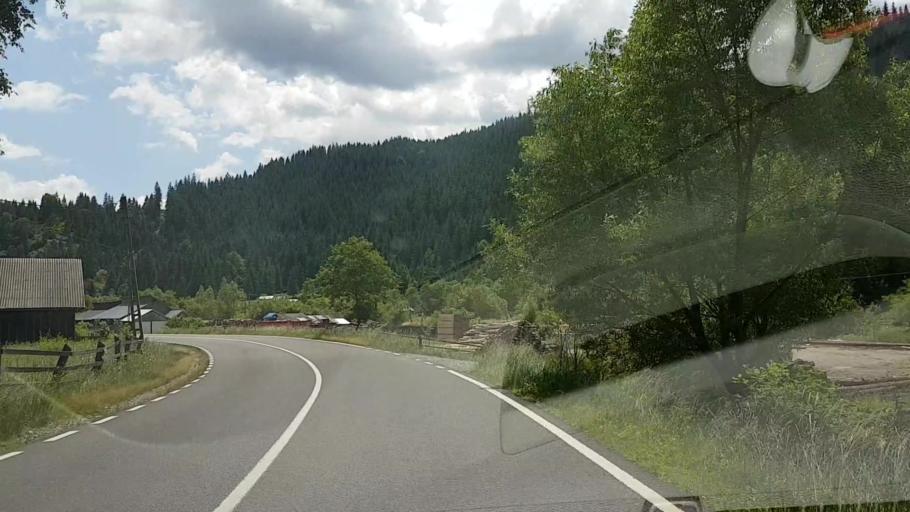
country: RO
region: Suceava
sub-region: Comuna Crucea
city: Crucea
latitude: 47.3957
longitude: 25.5637
